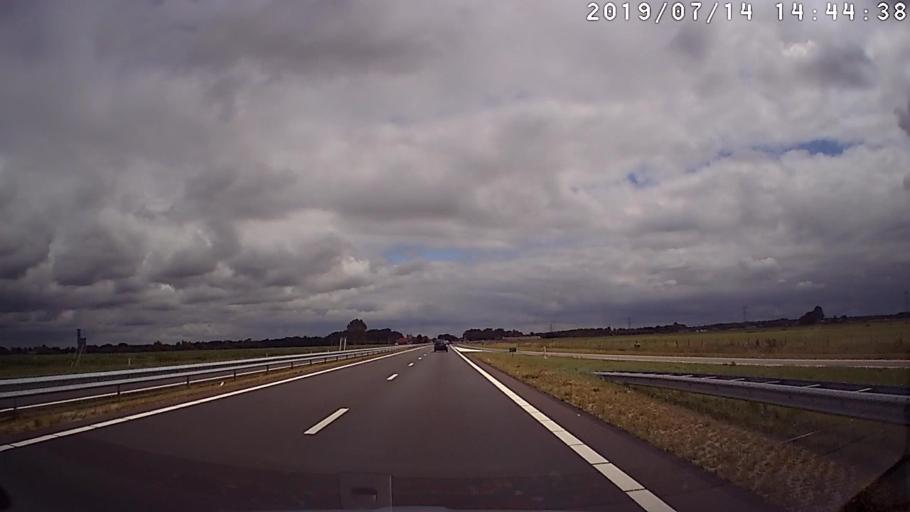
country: NL
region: Overijssel
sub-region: Gemeente Raalte
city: Heino
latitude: 52.4824
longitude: 6.1797
